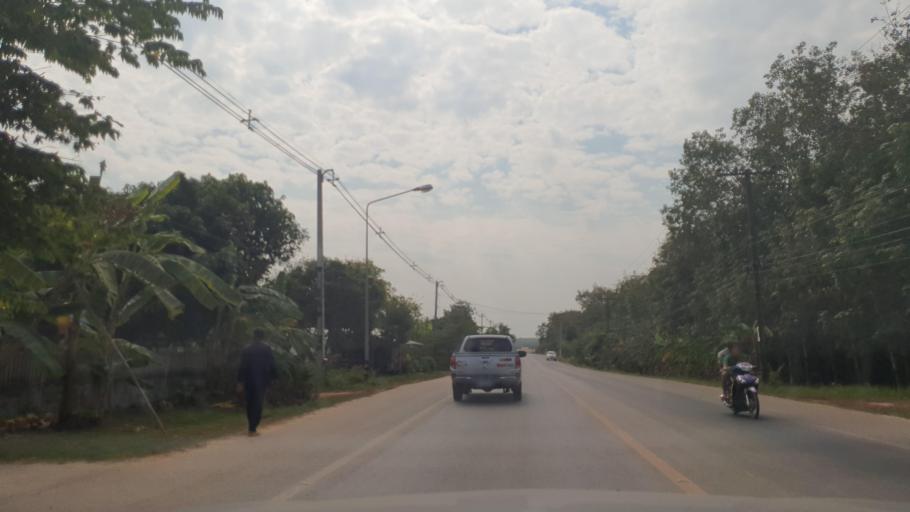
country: TH
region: Changwat Bueng Kan
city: Si Wilai
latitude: 18.2980
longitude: 103.8021
